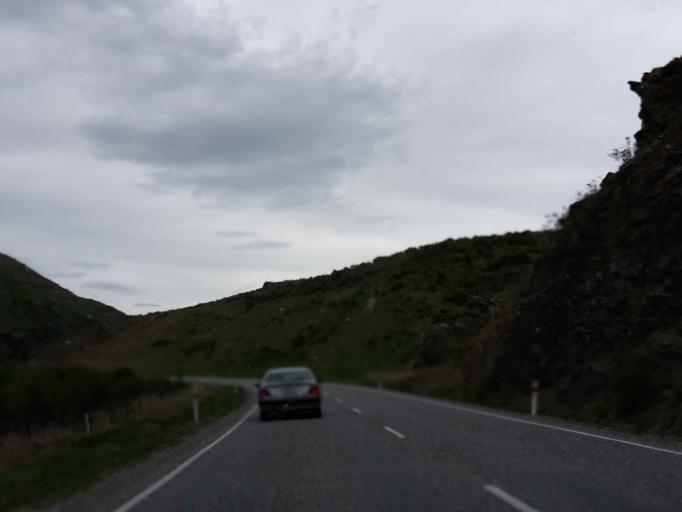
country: NZ
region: Otago
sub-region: Queenstown-Lakes District
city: Wanaka
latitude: -44.7409
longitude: 169.5098
